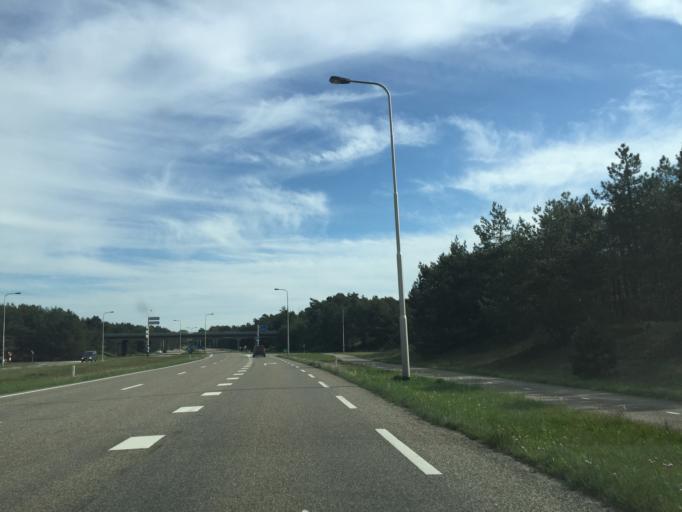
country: NL
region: Gelderland
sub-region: Gemeente Apeldoorn
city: Uddel
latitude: 52.2013
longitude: 5.7777
